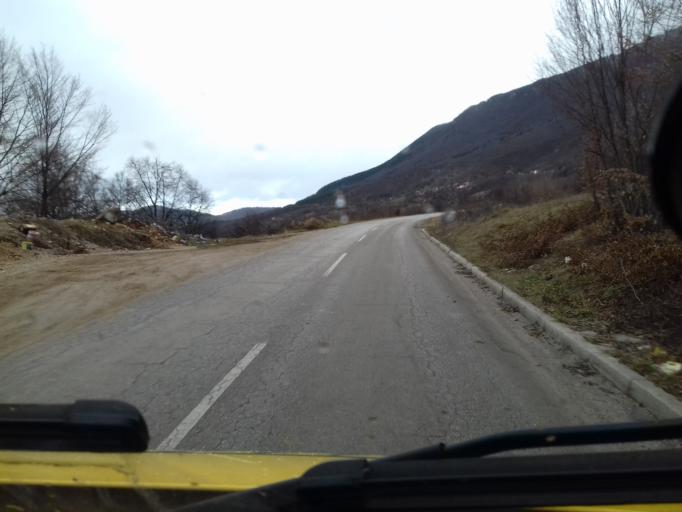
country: BA
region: Federation of Bosnia and Herzegovina
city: Turbe
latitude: 44.2520
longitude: 17.5566
